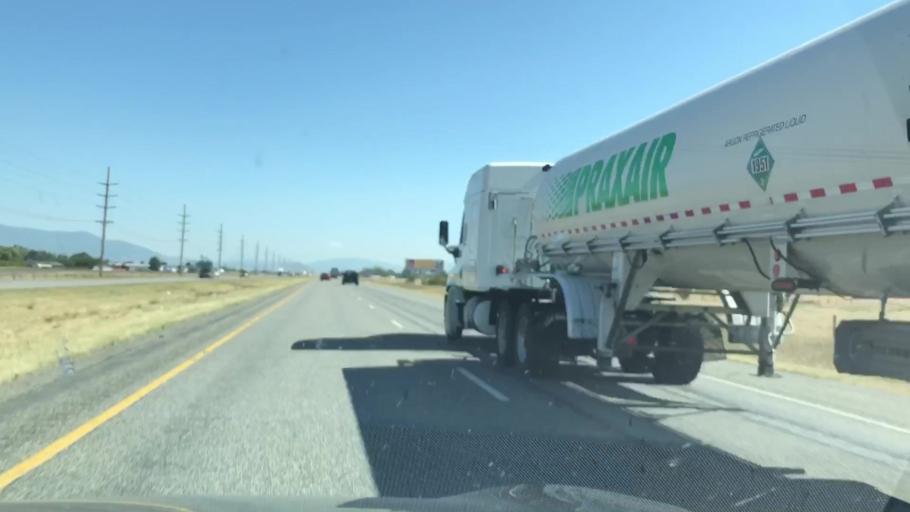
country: US
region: Montana
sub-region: Gallatin County
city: Belgrade
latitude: 45.8067
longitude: -111.2415
